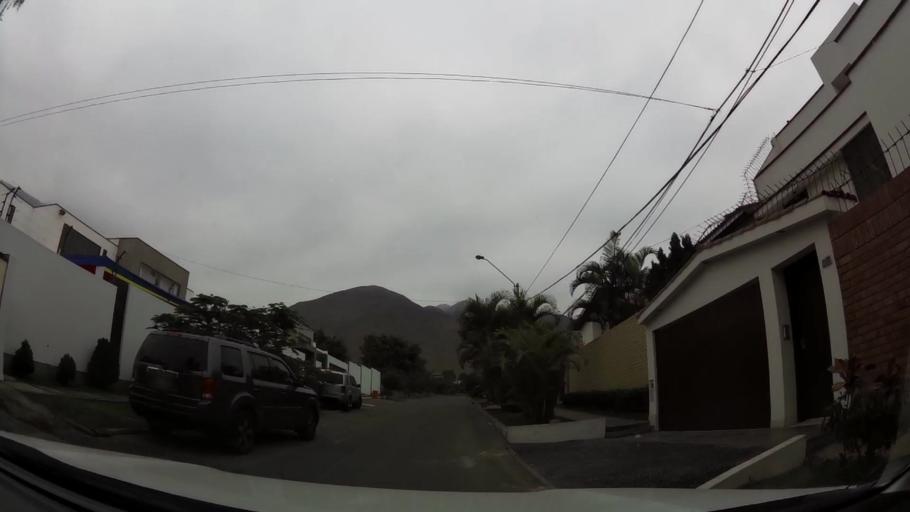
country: PE
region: Lima
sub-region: Lima
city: La Molina
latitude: -12.0935
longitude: -76.9249
